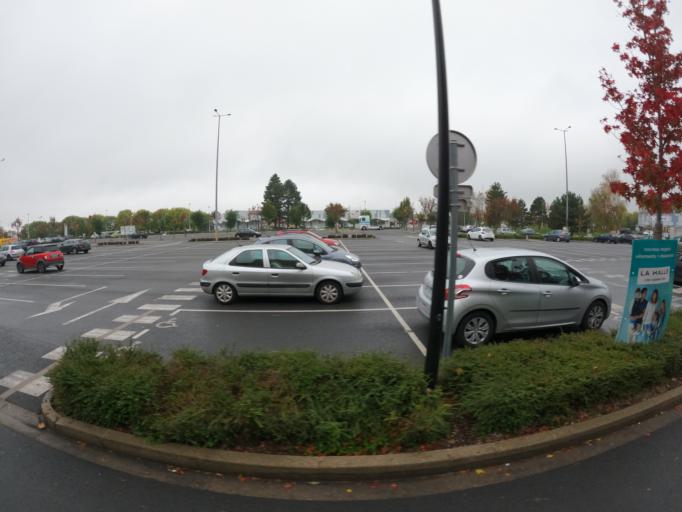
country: FR
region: Ile-de-France
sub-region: Departement du Val-de-Marne
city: Ormesson-sur-Marne
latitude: 48.7926
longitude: 2.5589
